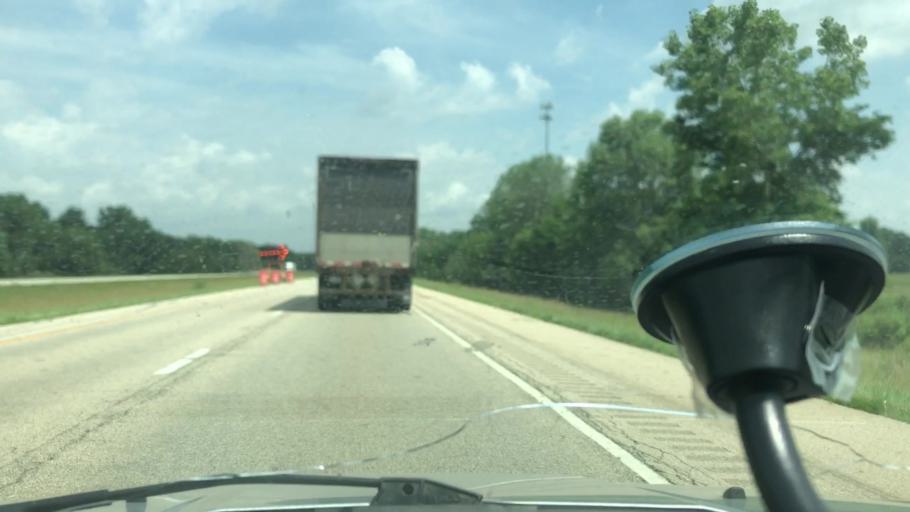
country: US
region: Illinois
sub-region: Peoria County
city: Bellevue
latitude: 40.7153
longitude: -89.6761
